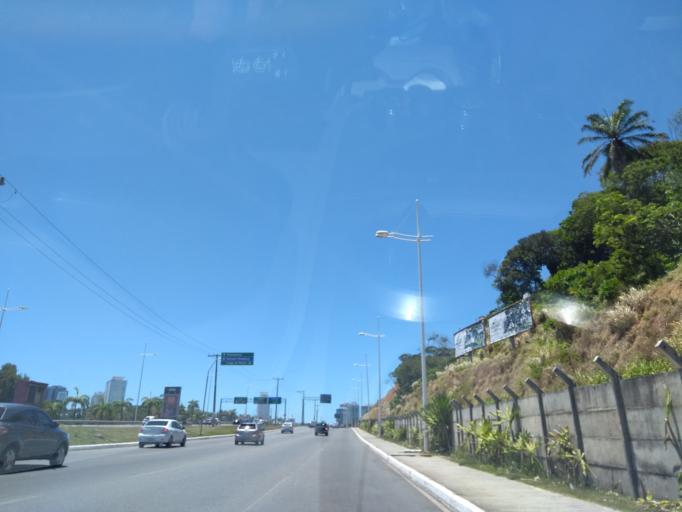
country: BR
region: Bahia
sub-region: Salvador
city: Salvador
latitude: -12.9708
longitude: -38.4456
